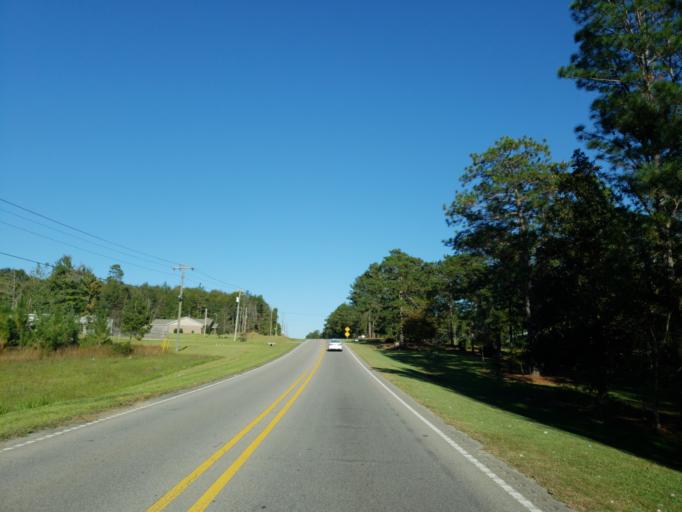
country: US
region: Mississippi
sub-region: Forrest County
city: Petal
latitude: 31.3531
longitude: -89.1705
